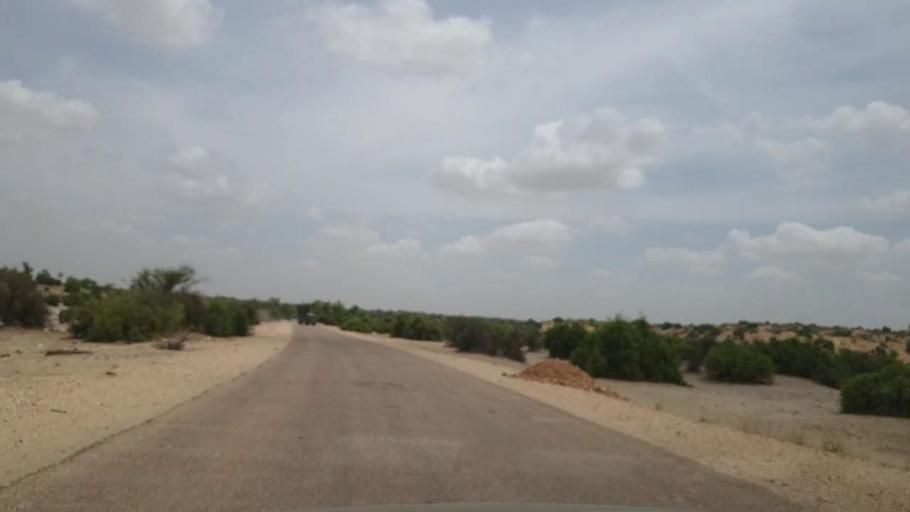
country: PK
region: Sindh
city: Kot Diji
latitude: 27.1825
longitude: 69.1724
